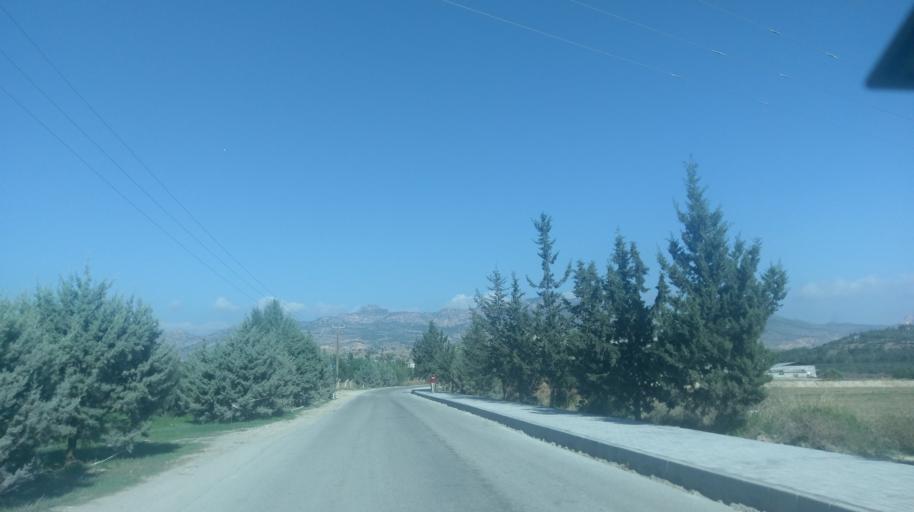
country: CY
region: Lefkosia
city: Nicosia
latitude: 35.2250
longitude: 33.4183
